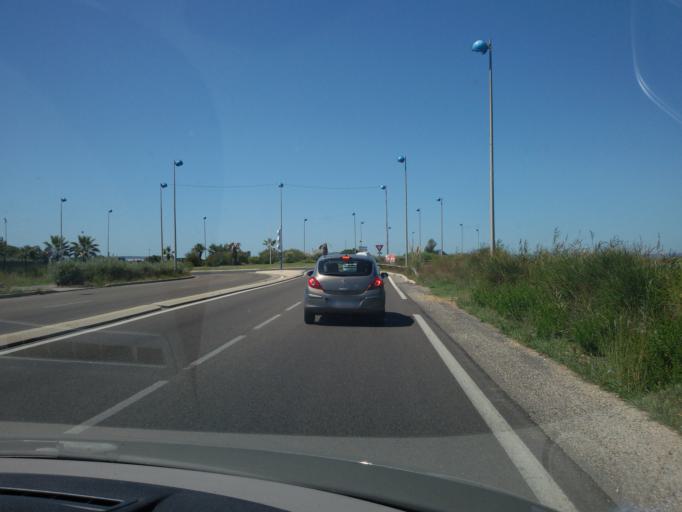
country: FR
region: Languedoc-Roussillon
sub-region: Departement de l'Herault
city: Palavas-les-Flots
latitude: 43.5348
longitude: 3.9397
